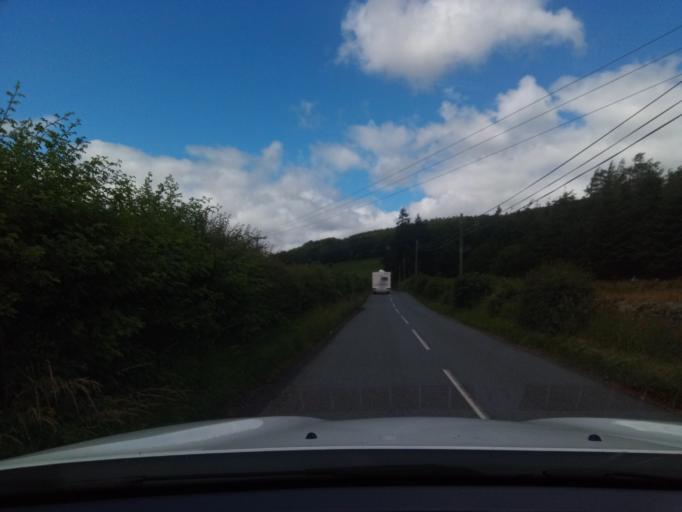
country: GB
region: Scotland
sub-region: The Scottish Borders
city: Innerleithen
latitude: 55.5558
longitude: -2.9608
